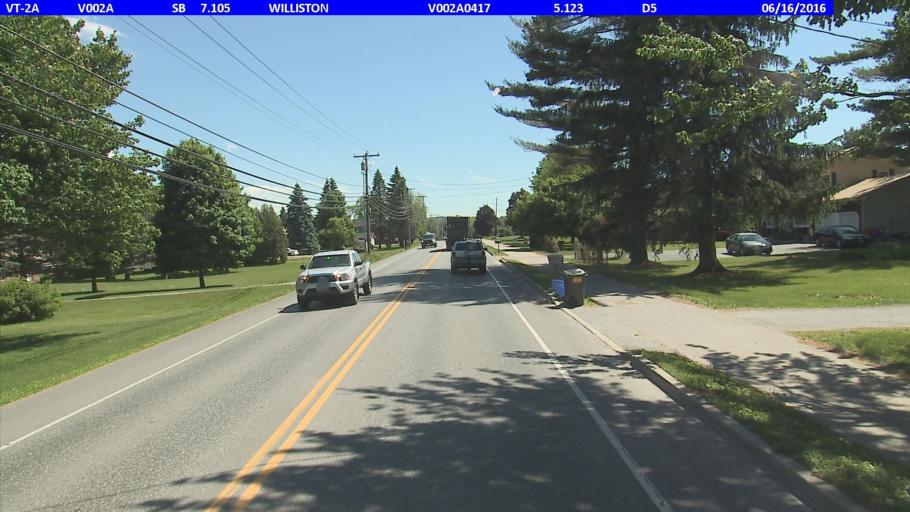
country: US
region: Vermont
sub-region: Chittenden County
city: Essex Junction
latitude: 44.4698
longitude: -73.1131
